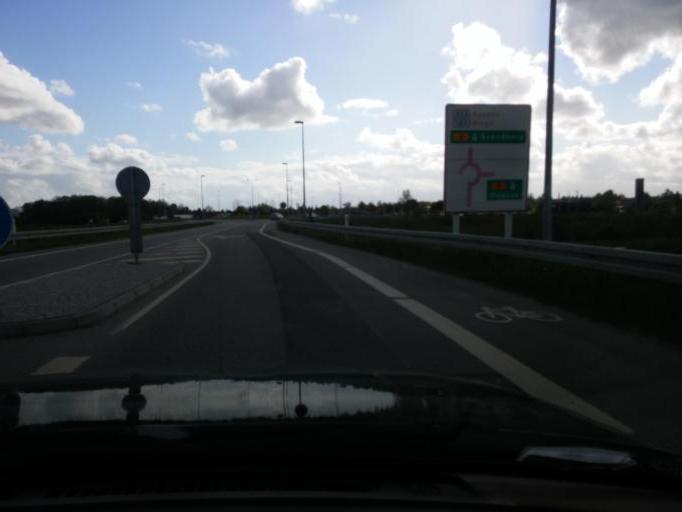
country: DK
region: South Denmark
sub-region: Faaborg-Midtfyn Kommune
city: Ringe
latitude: 55.2379
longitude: 10.4953
